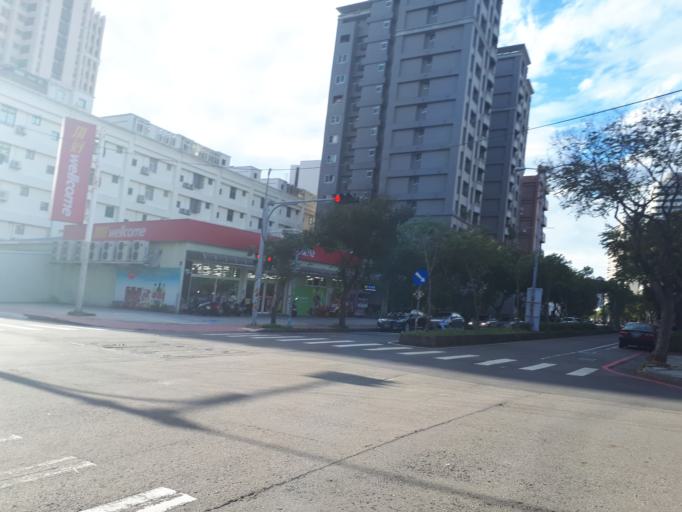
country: TW
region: Taiwan
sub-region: Hsinchu
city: Zhubei
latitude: 24.8031
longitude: 121.0362
